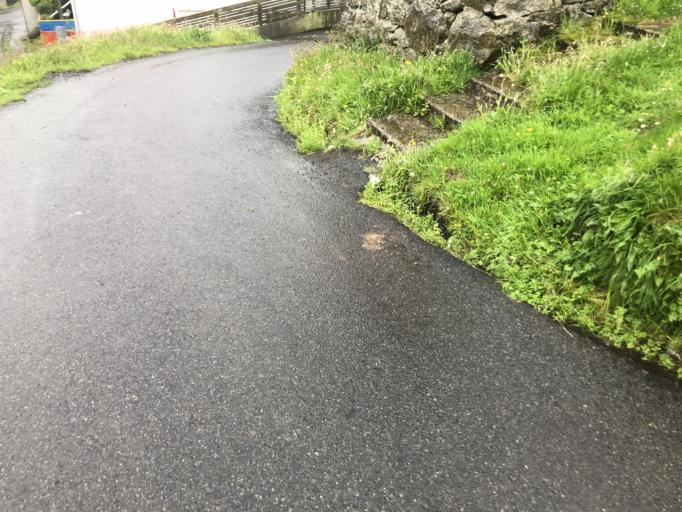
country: FO
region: Sandoy
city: Sandur
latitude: 61.7714
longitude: -6.8059
